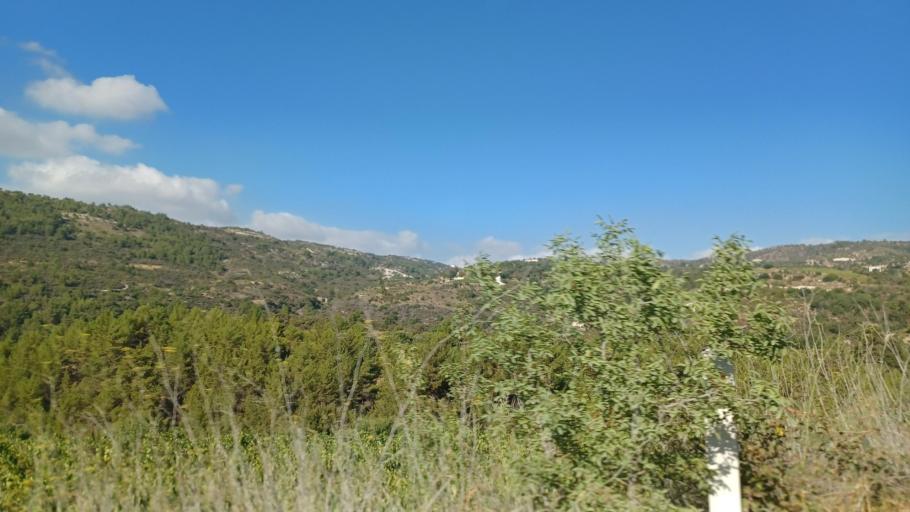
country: CY
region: Limassol
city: Pachna
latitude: 34.8424
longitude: 32.7136
